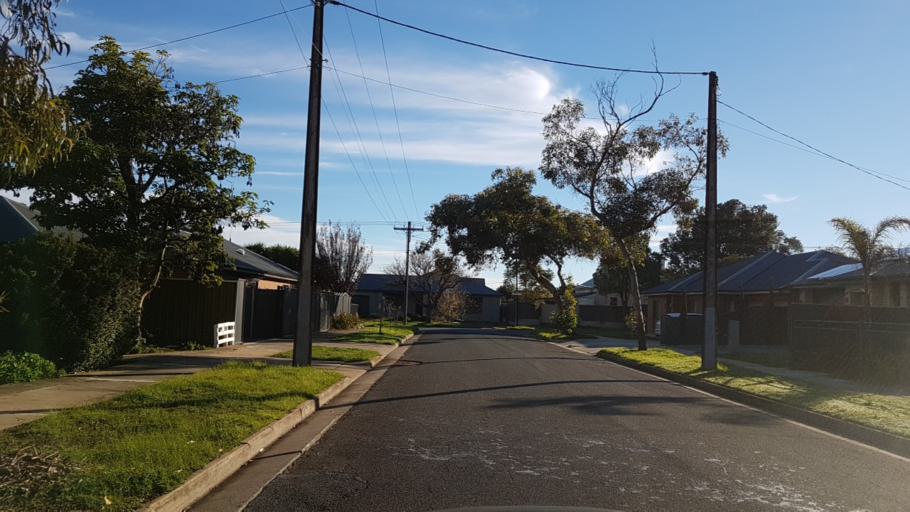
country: AU
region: South Australia
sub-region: Charles Sturt
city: Woodville West
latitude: -34.8940
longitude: 138.5248
